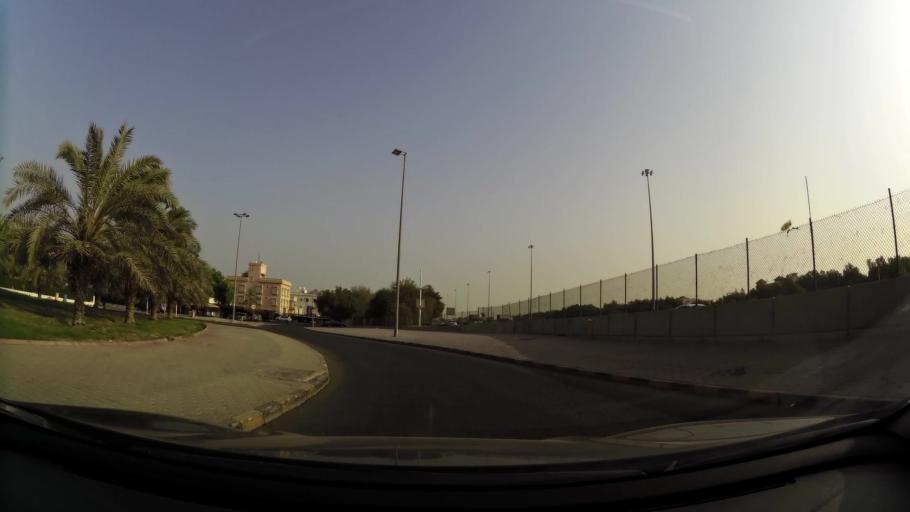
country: KW
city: Bayan
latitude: 29.3097
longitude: 48.0571
